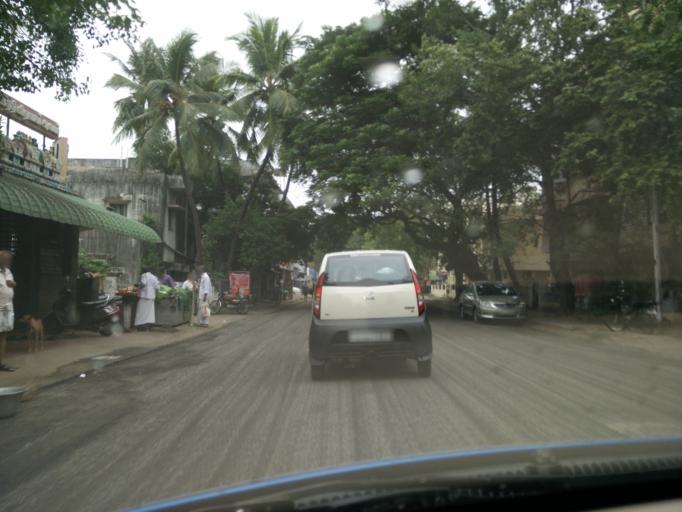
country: IN
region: Tamil Nadu
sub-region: Chennai
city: Gandhi Nagar
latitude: 13.0002
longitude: 80.2519
